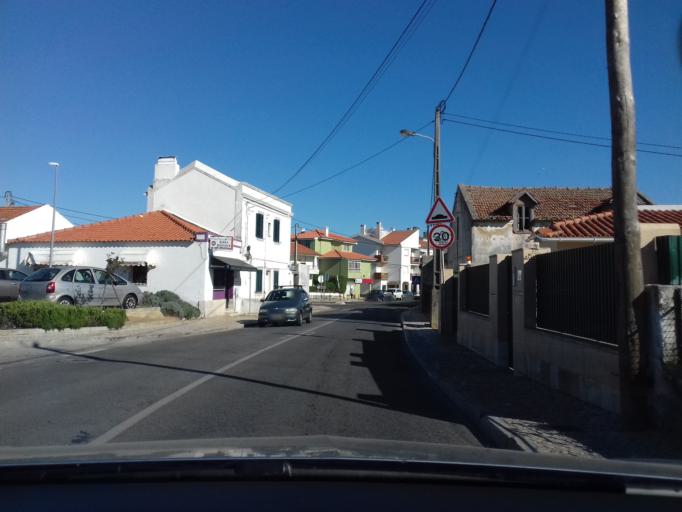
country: PT
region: Lisbon
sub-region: Cascais
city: Alcabideche
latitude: 38.7198
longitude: -9.4103
